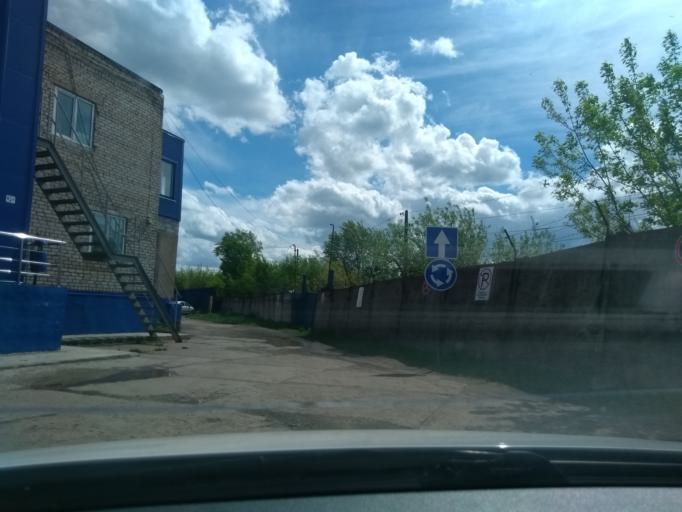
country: RU
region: Perm
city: Kondratovo
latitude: 58.0075
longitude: 56.0862
